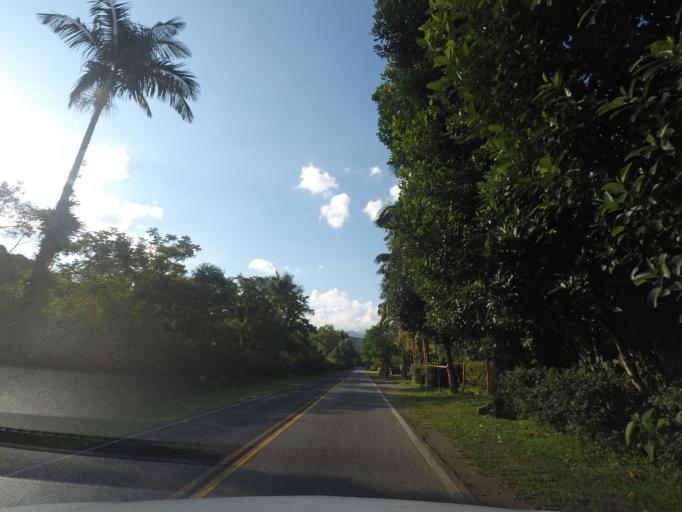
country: BR
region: Parana
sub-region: Antonina
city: Antonina
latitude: -25.4024
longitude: -48.8725
